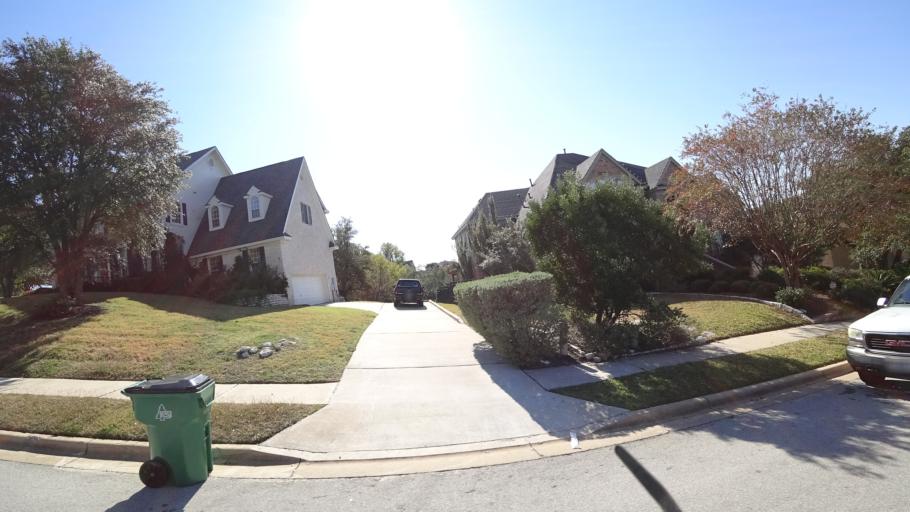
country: US
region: Texas
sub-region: Travis County
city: Lost Creek
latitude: 30.3712
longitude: -97.8624
